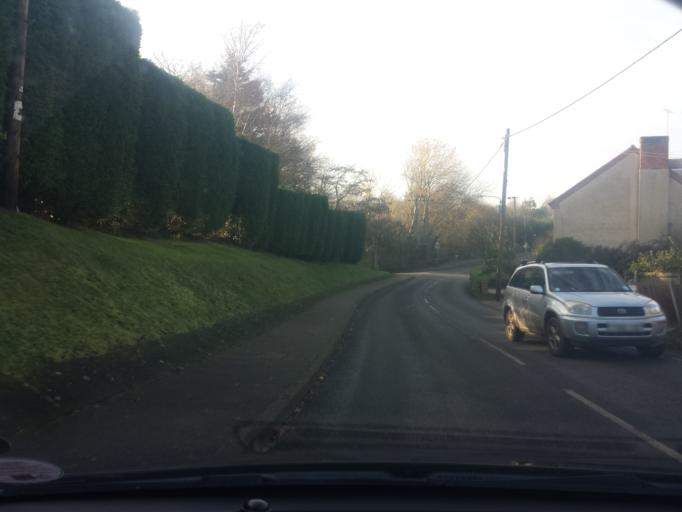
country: GB
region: England
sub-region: Essex
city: Saint Osyth
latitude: 51.7957
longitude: 1.0837
